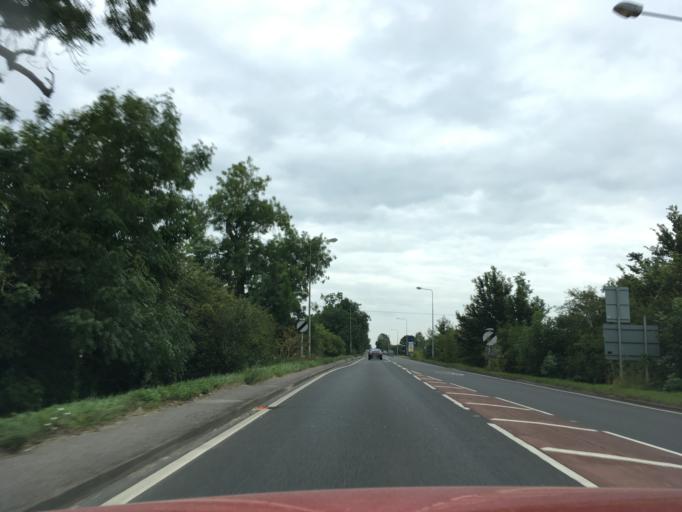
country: GB
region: England
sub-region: Central Bedfordshire
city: Hockliffe
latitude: 51.9231
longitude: -0.5742
